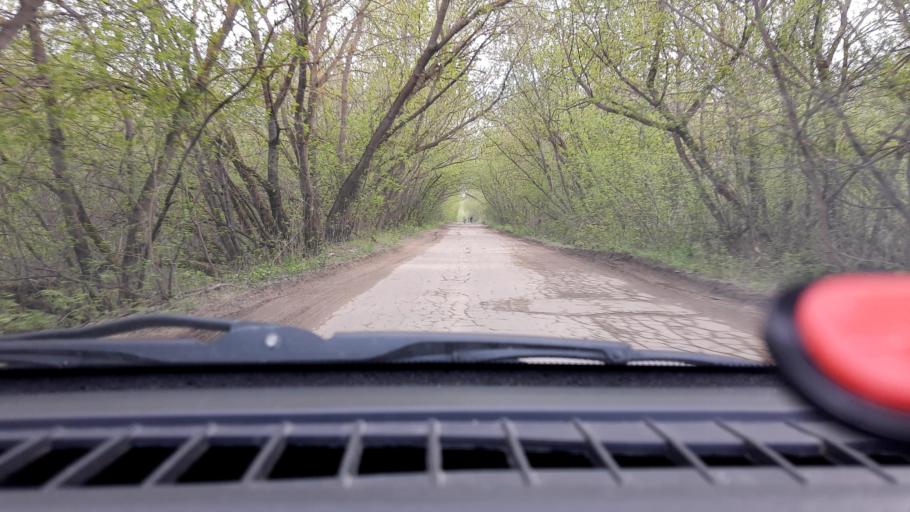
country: RU
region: Nizjnij Novgorod
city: Neklyudovo
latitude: 56.3892
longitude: 43.8421
